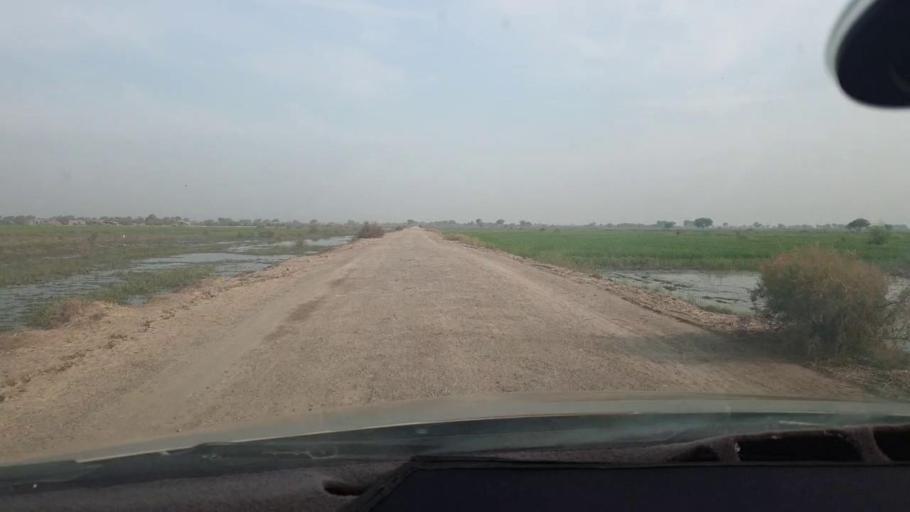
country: PK
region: Balochistan
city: Jhatpat
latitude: 28.3592
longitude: 68.4075
